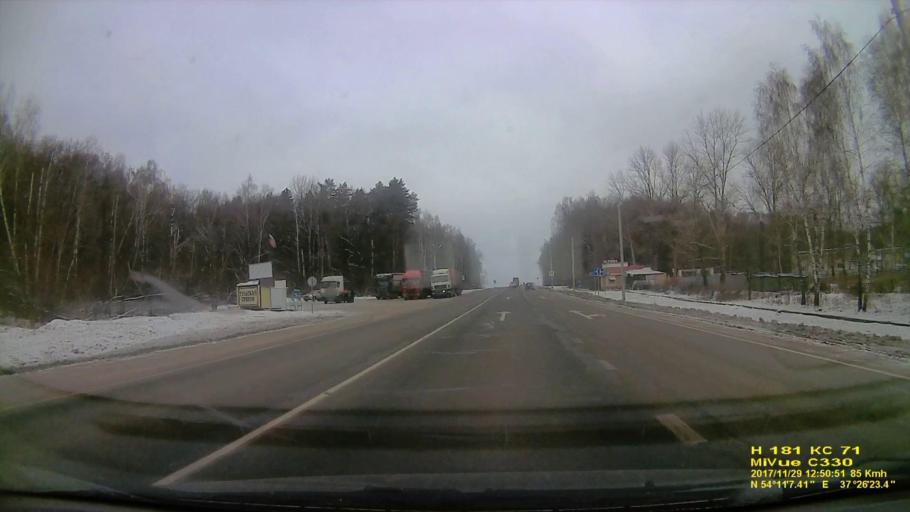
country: RU
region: Tula
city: Barsuki
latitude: 54.1855
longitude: 37.4396
